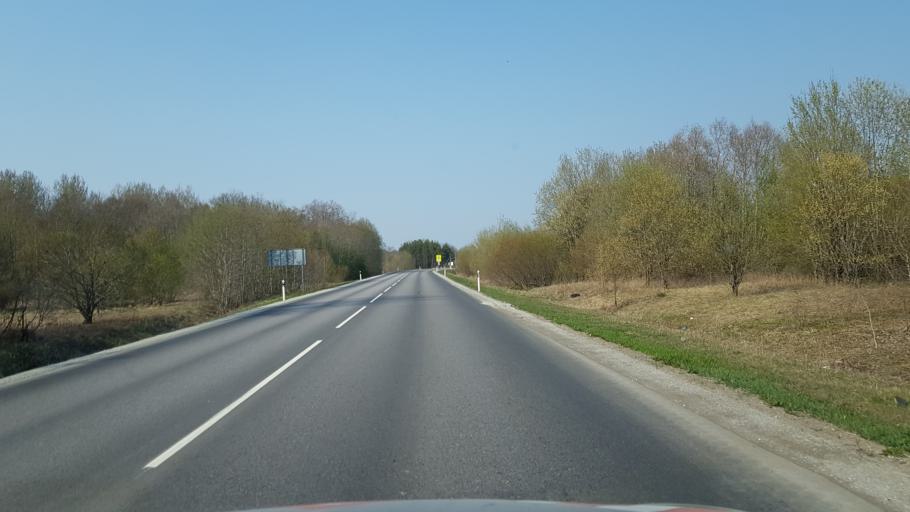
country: EE
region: Harju
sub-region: Paldiski linn
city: Paldiski
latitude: 59.3334
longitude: 24.1027
